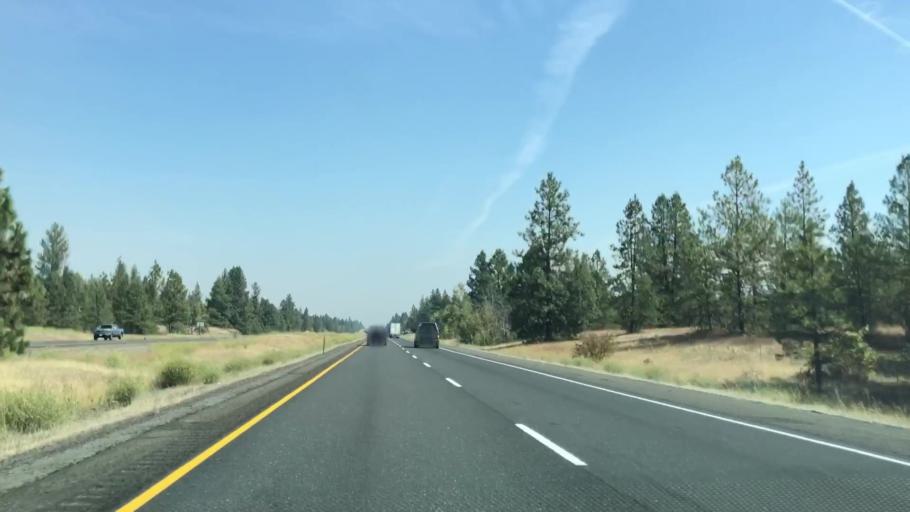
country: US
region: Washington
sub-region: Spokane County
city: Medical Lake
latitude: 47.4665
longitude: -117.7500
